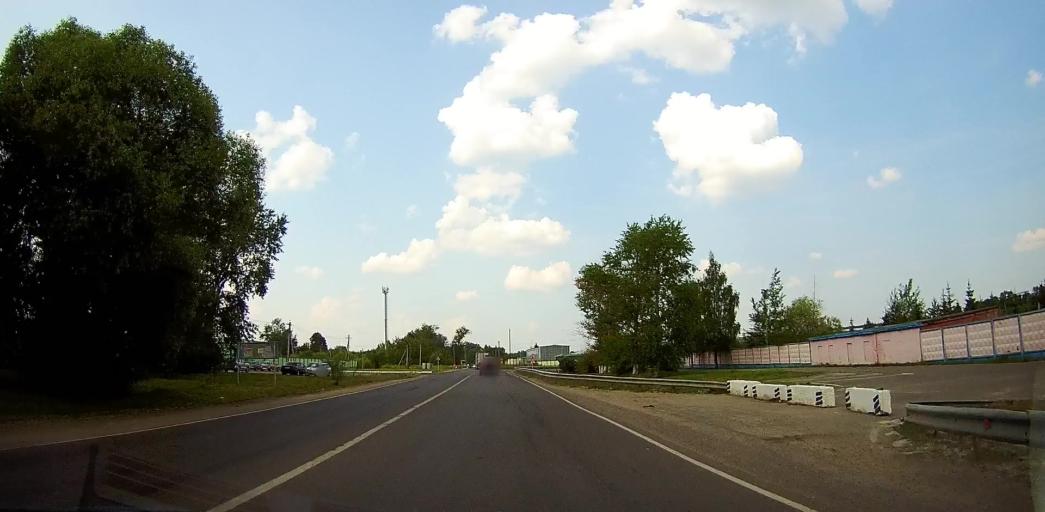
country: RU
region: Moskovskaya
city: Mikhnevo
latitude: 55.1360
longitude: 37.9496
